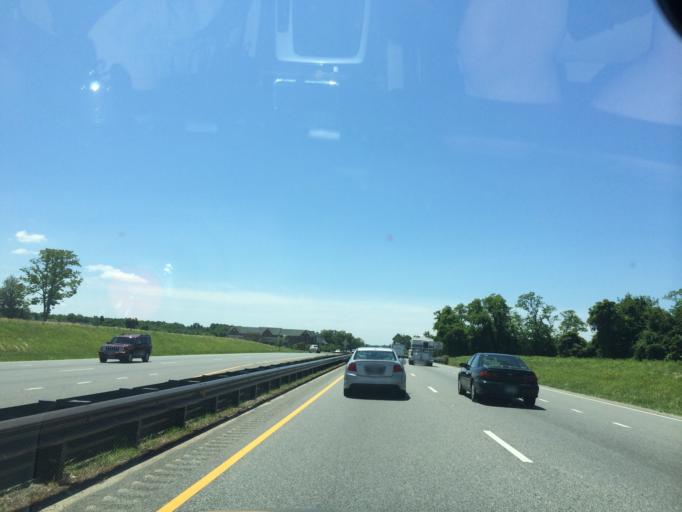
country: US
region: Maryland
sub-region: Talbot County
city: Easton
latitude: 38.7924
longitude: -76.0602
